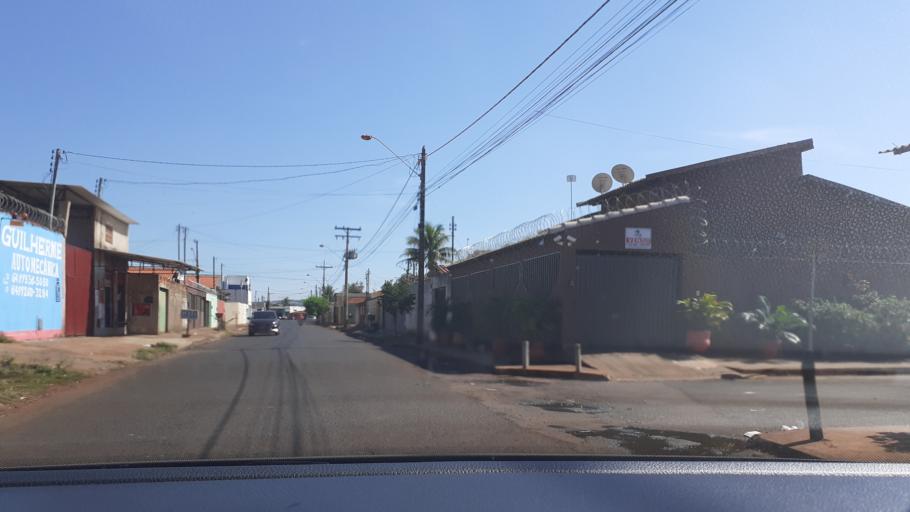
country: BR
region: Goias
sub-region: Itumbiara
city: Itumbiara
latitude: -18.4146
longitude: -49.2524
